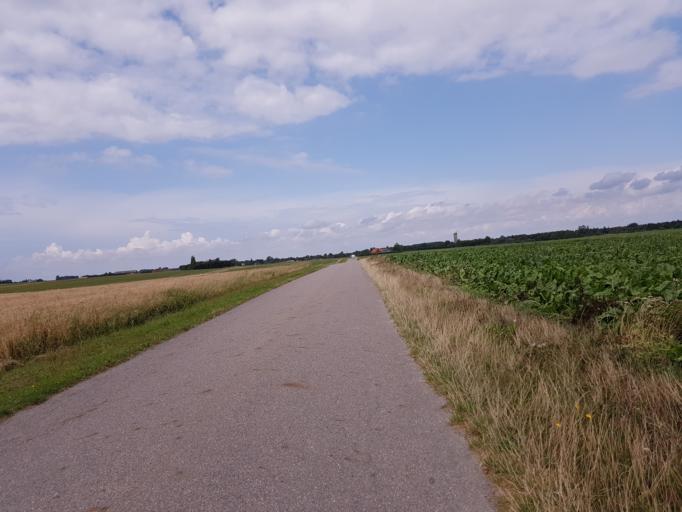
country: DK
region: Zealand
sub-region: Guldborgsund Kommune
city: Nykobing Falster
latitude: 54.5896
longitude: 11.9537
